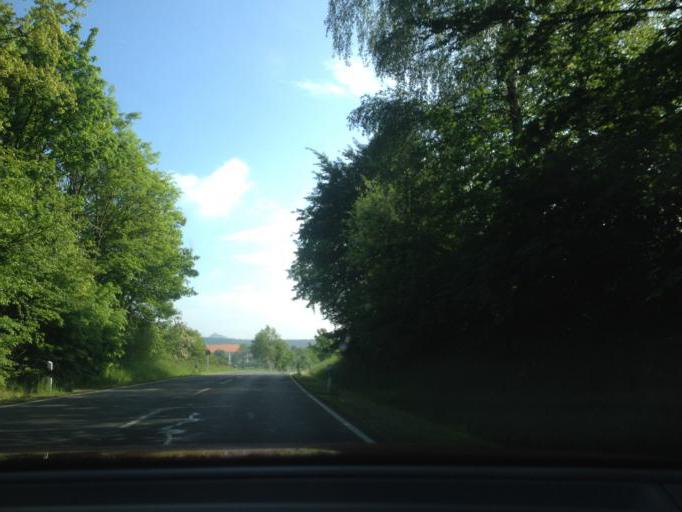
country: DE
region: Bavaria
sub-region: Upper Palatinate
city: Speinshart
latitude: 49.7802
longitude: 11.8160
